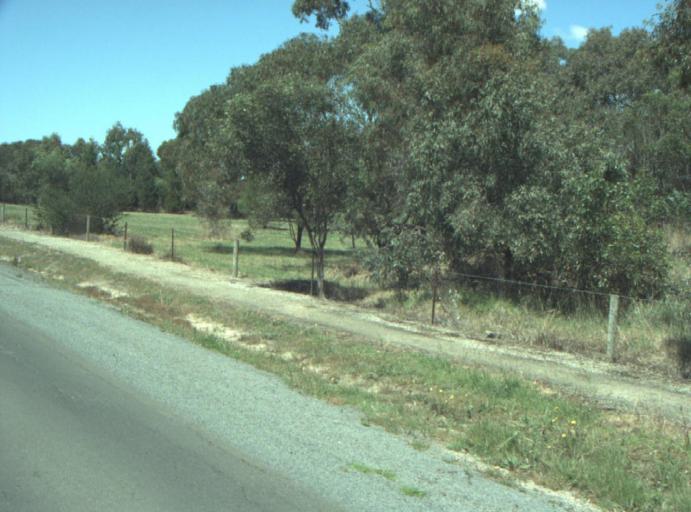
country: AU
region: Victoria
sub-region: Greater Geelong
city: Breakwater
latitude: -38.2025
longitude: 144.3618
